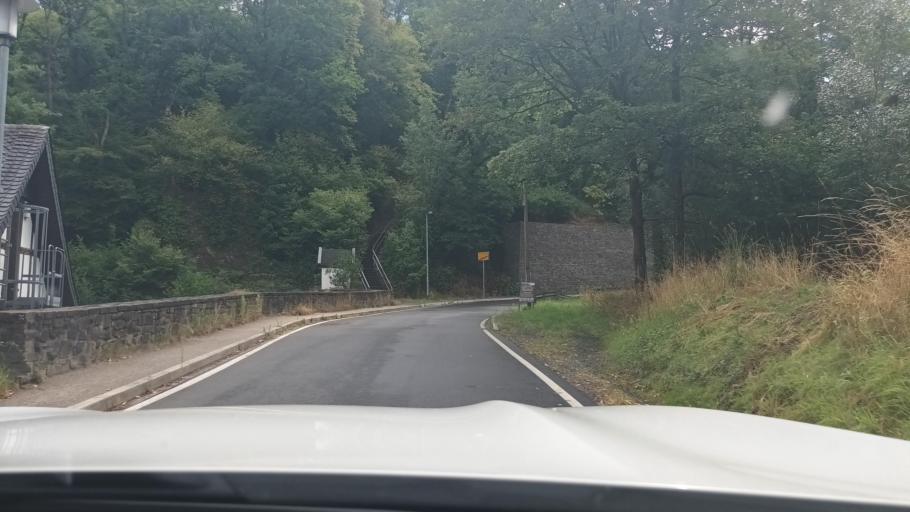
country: DE
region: North Rhine-Westphalia
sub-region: Regierungsbezirk Koln
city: Hennef
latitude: 50.7648
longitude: 7.3562
